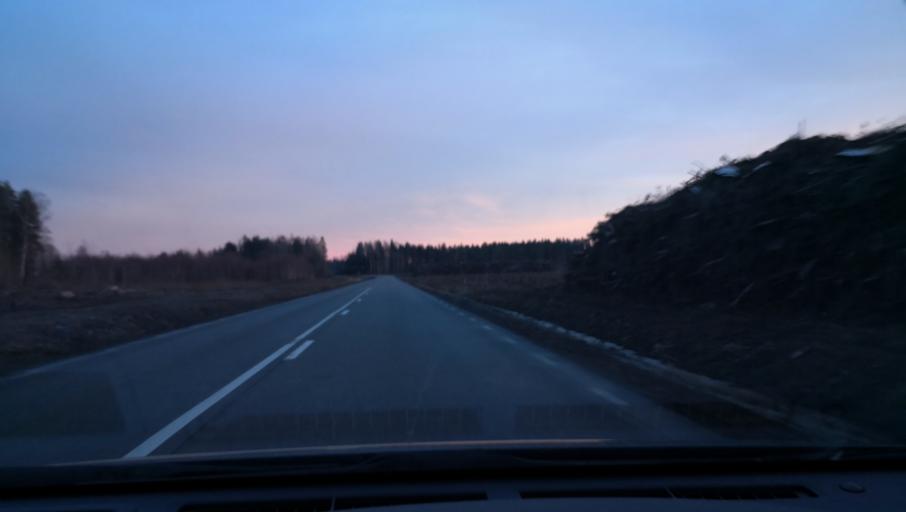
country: SE
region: OErebro
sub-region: Orebro Kommun
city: Orebro
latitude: 59.2374
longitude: 15.1090
